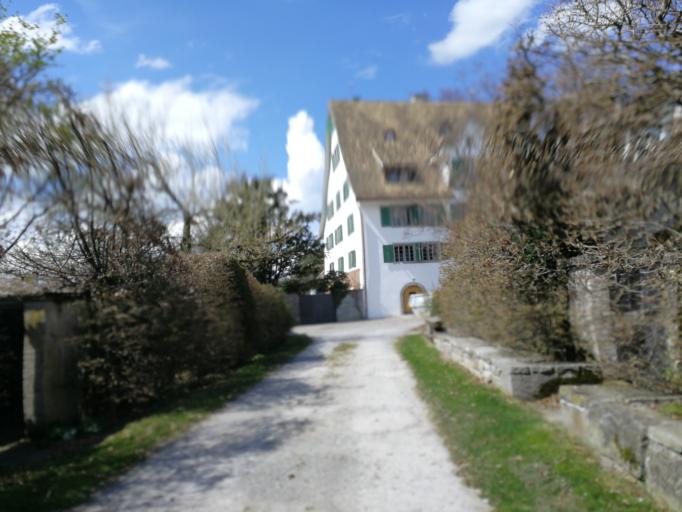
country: CH
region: Zurich
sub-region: Bezirk Meilen
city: Hombrechtikon
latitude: 47.2339
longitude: 8.7780
